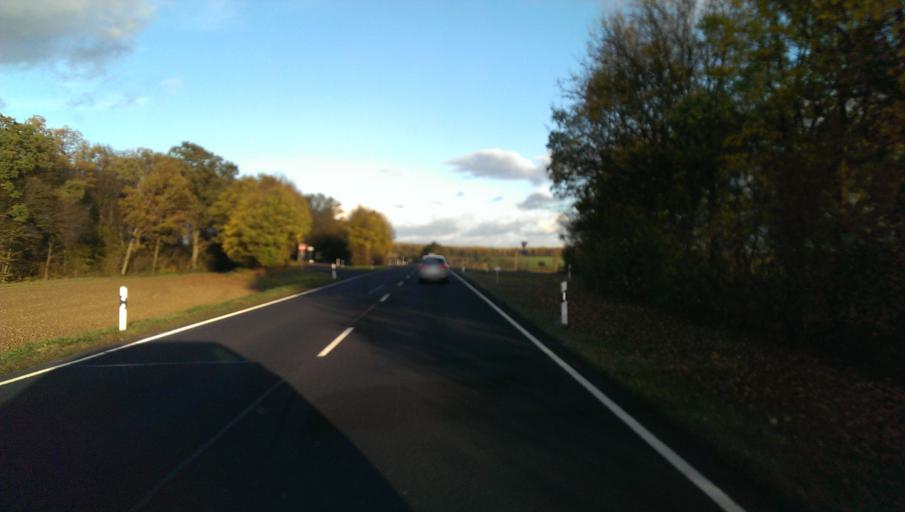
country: DE
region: Bavaria
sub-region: Regierungsbezirk Unterfranken
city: Arnstein
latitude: 50.0042
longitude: 10.0288
